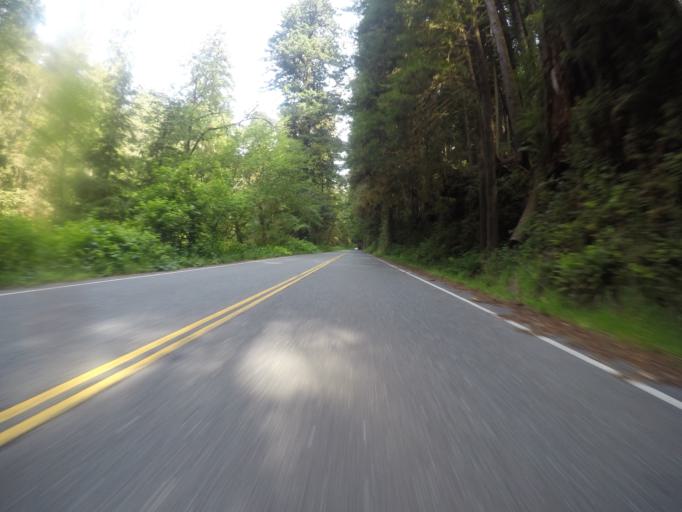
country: US
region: California
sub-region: Del Norte County
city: Bertsch-Oceanview
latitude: 41.4174
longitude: -124.0329
